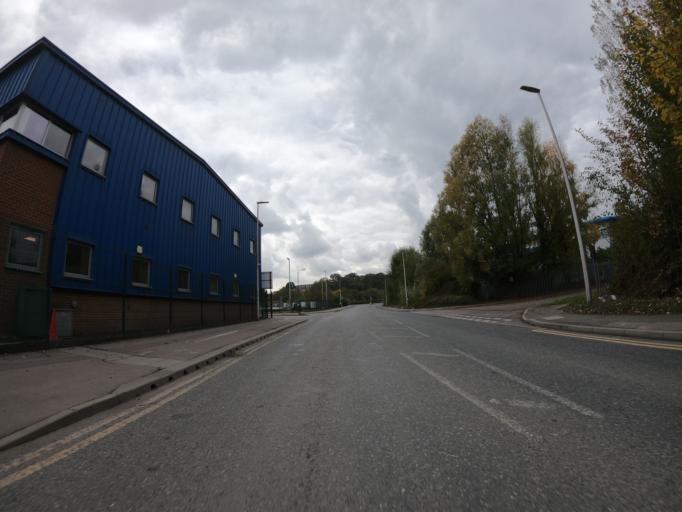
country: GB
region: England
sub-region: Greater London
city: Erith
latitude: 51.4898
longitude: 0.1687
